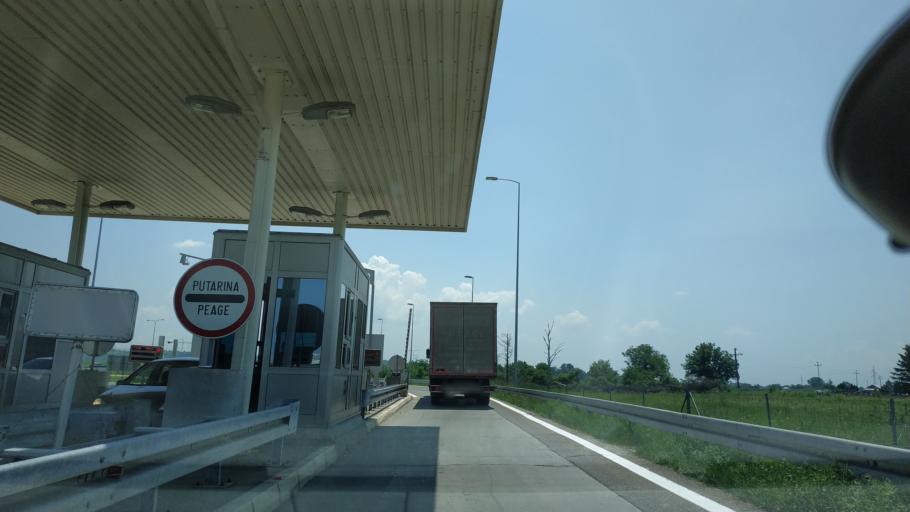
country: RS
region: Central Serbia
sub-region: Pomoravski Okrug
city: Cuprija
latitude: 43.9343
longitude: 21.3889
